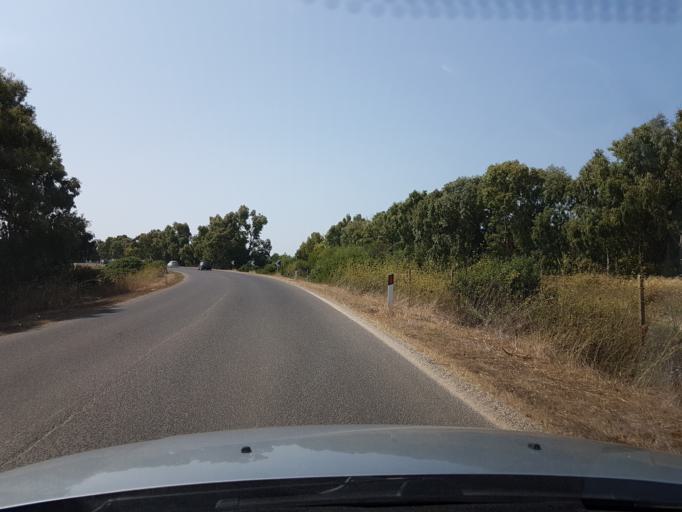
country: IT
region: Sardinia
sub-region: Provincia di Oristano
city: Cabras
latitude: 39.9181
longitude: 8.4969
